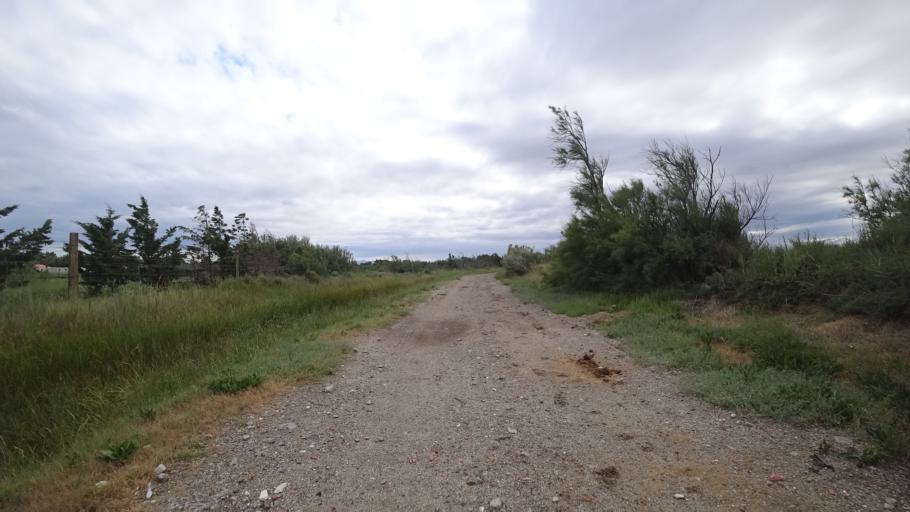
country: FR
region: Languedoc-Roussillon
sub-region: Departement des Pyrenees-Orientales
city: Le Barcares
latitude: 42.7810
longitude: 3.0195
